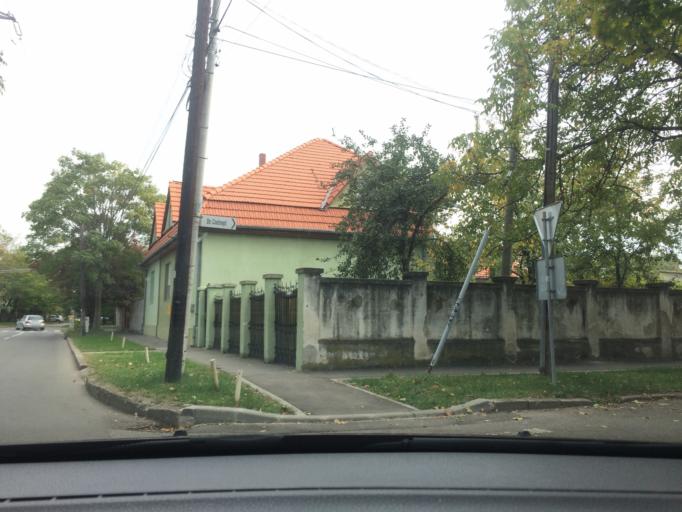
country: RO
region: Timis
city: Timisoara
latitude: 45.7552
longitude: 21.2085
